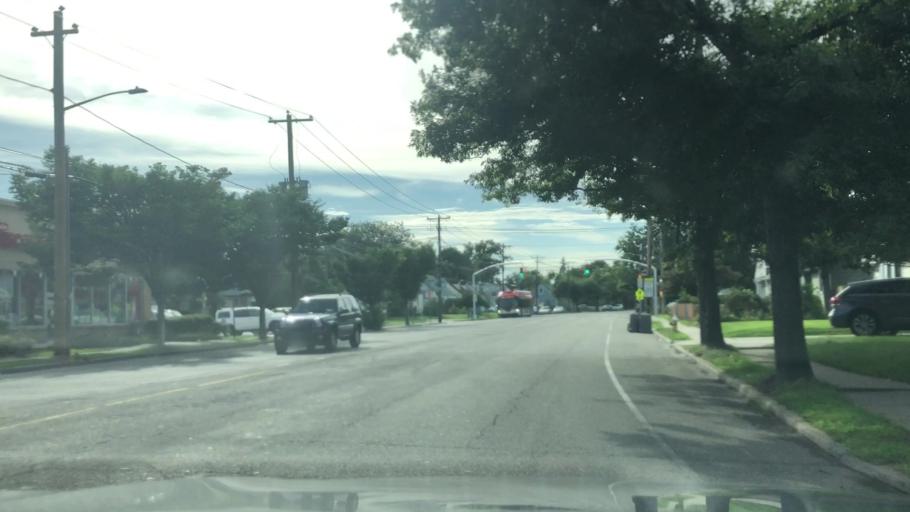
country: US
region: New York
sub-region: Nassau County
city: Uniondale
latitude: 40.6944
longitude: -73.5799
